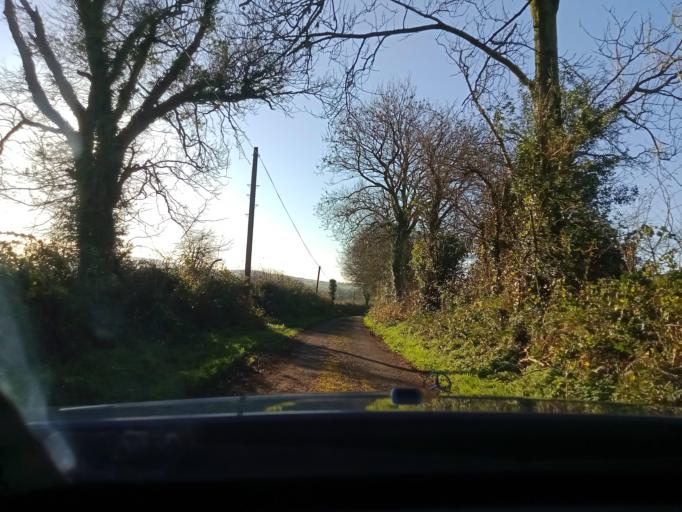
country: IE
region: Munster
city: Carrick-on-Suir
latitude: 52.4461
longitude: -7.4172
